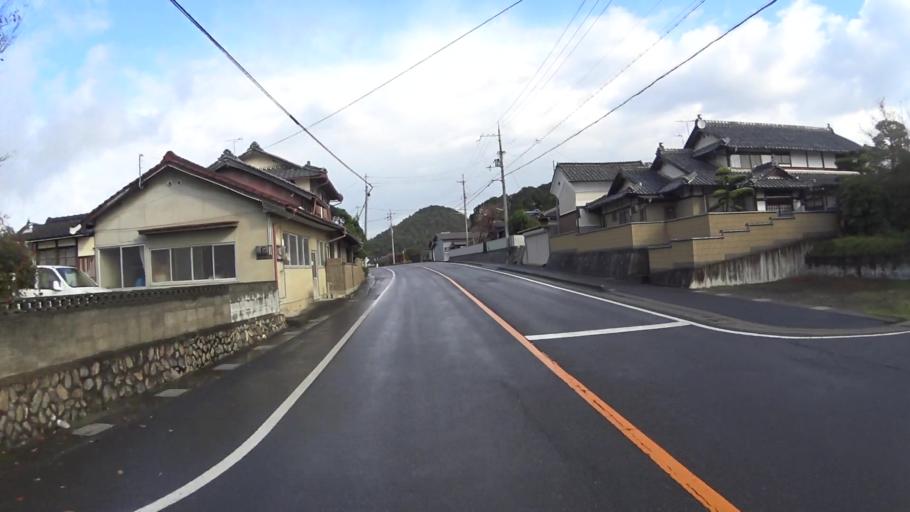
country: JP
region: Kyoto
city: Ayabe
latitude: 35.3270
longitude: 135.2146
